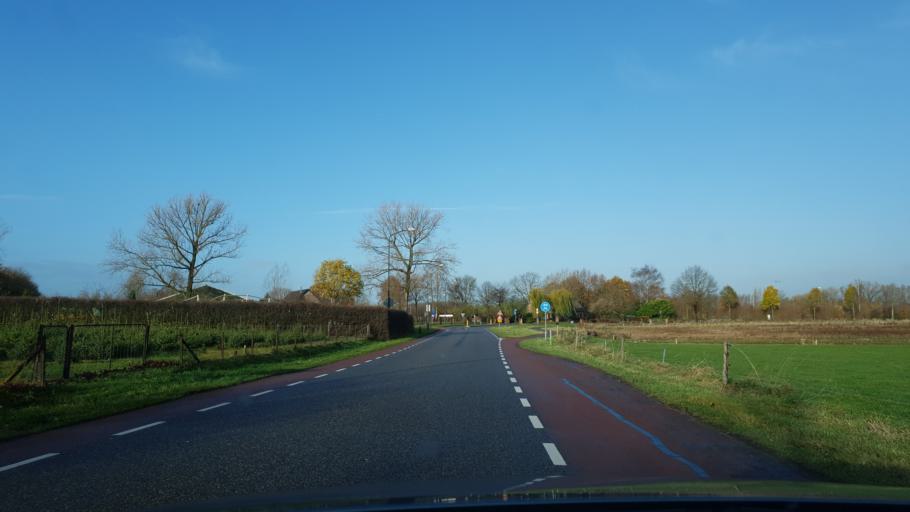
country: NL
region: Gelderland
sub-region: Gemeente Wijchen
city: Bergharen
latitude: 51.8380
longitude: 5.6758
